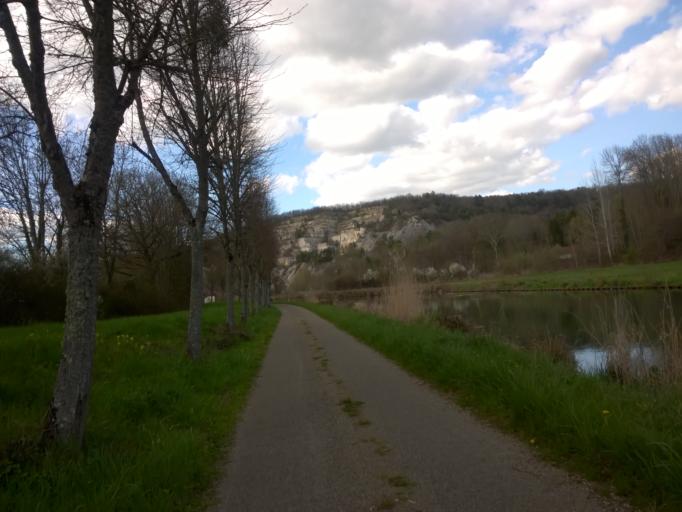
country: FR
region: Bourgogne
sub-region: Departement de l'Yonne
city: Ravieres
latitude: 47.7084
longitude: 4.2439
